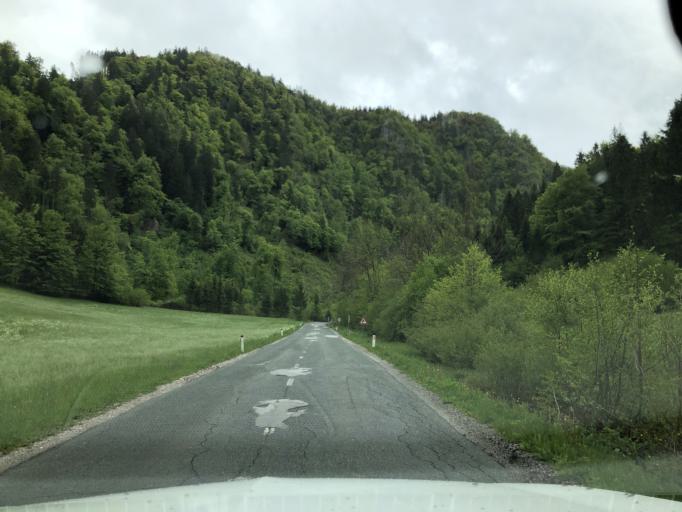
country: SI
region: Jesenice
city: Slovenski Javornik
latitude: 46.4064
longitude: 14.0781
